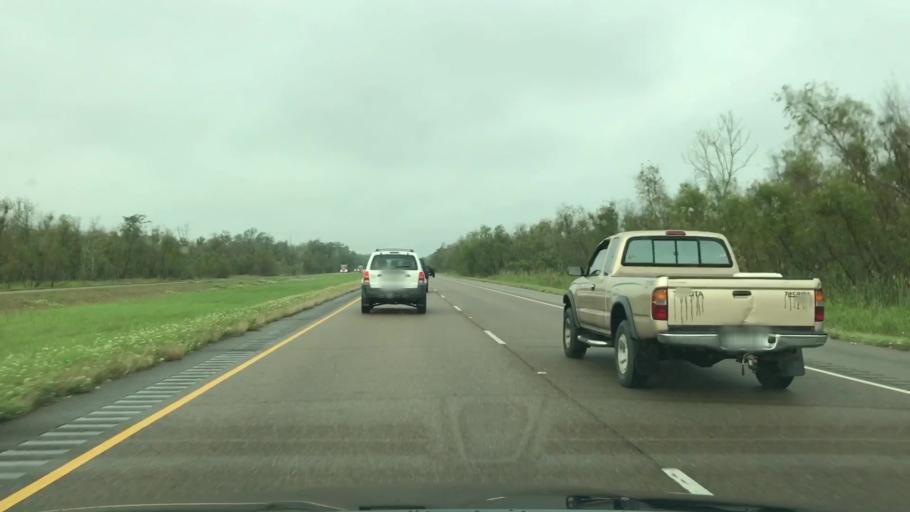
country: US
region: Louisiana
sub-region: Terrebonne Parish
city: Bayou Cane
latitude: 29.6863
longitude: -90.7116
